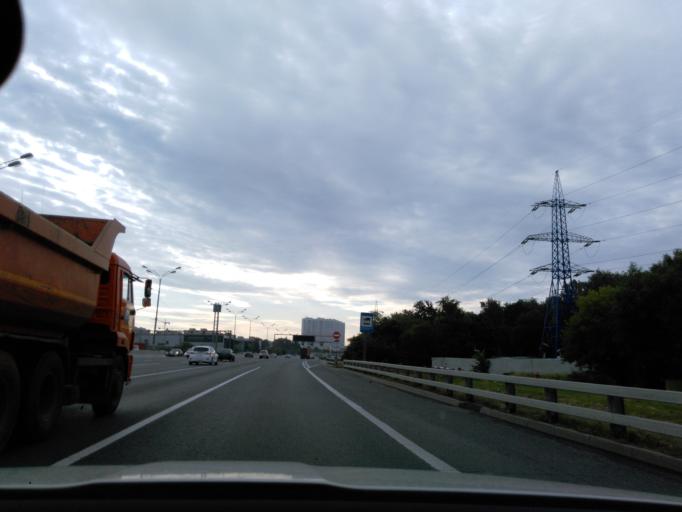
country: RU
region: Moscow
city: Vatutino
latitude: 55.8944
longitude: 37.6940
